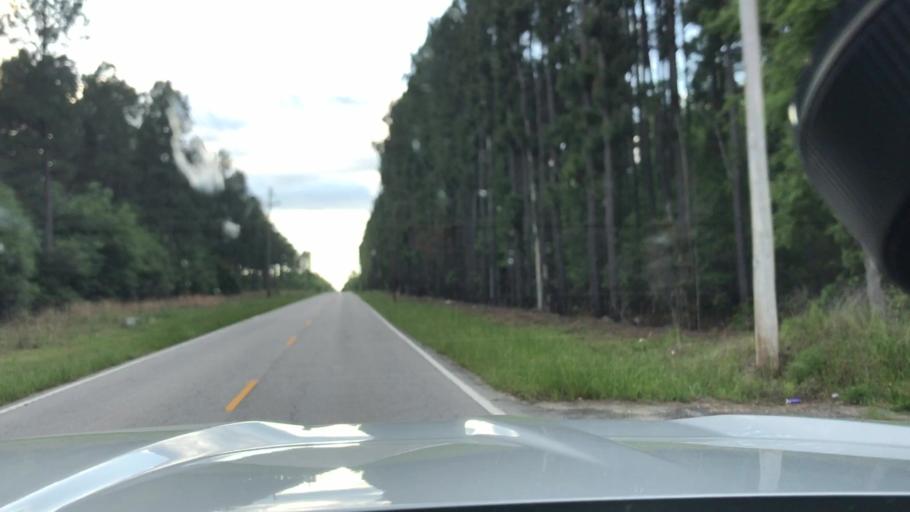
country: US
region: South Carolina
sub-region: Bamberg County
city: Denmark
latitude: 33.4598
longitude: -81.1492
